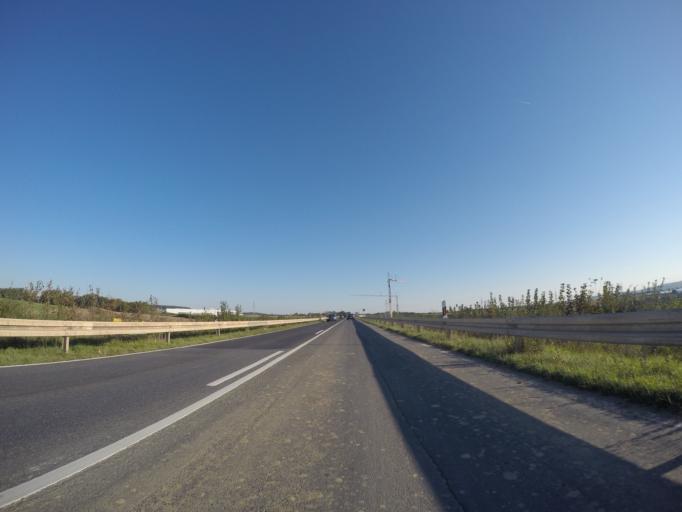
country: DE
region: Bavaria
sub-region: Regierungsbezirk Unterfranken
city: Esselbach
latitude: 49.8158
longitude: 9.5574
